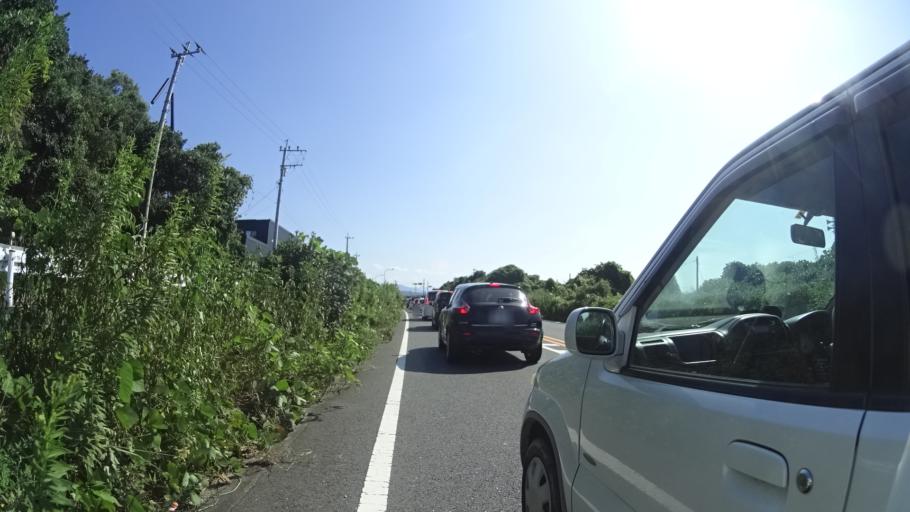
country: JP
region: Fukuoka
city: Yukuhashi
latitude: 33.6986
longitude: 130.9954
